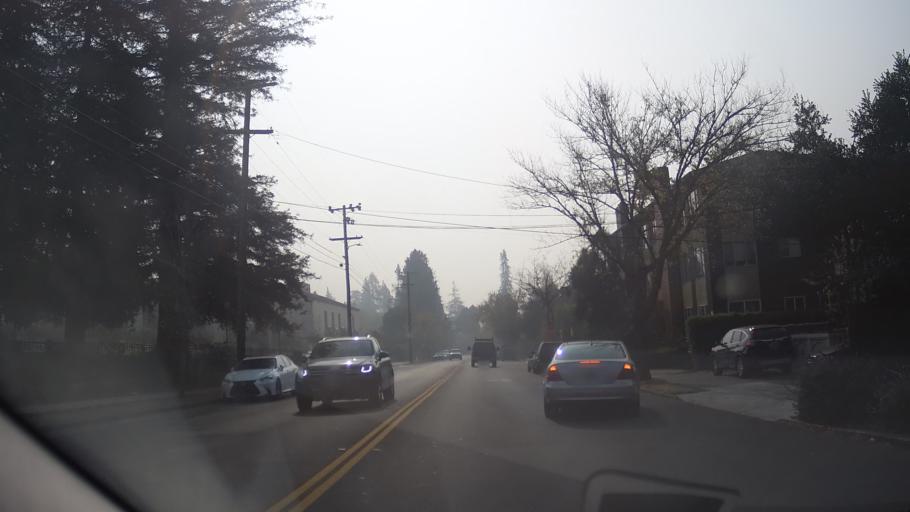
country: US
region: California
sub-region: Alameda County
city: Berkeley
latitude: 37.8649
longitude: -122.2504
